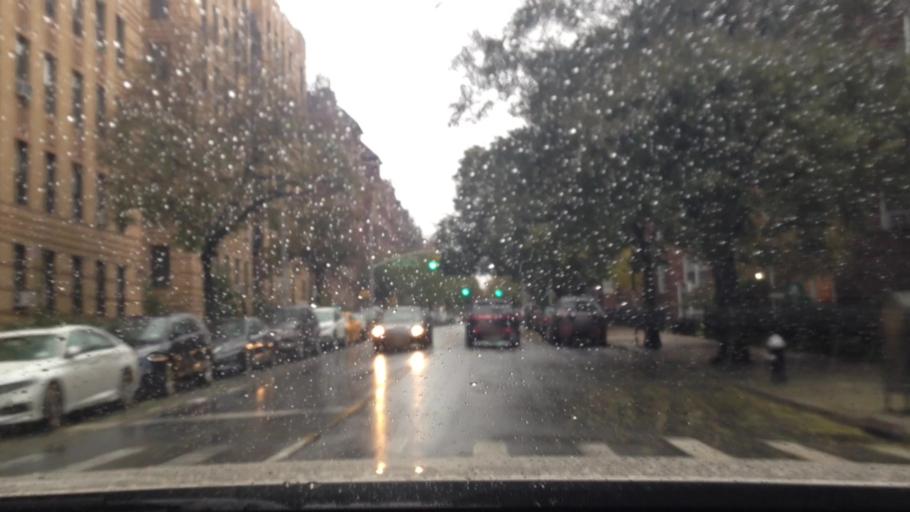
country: US
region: New York
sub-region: Queens County
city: Long Island City
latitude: 40.7510
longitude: -73.8930
